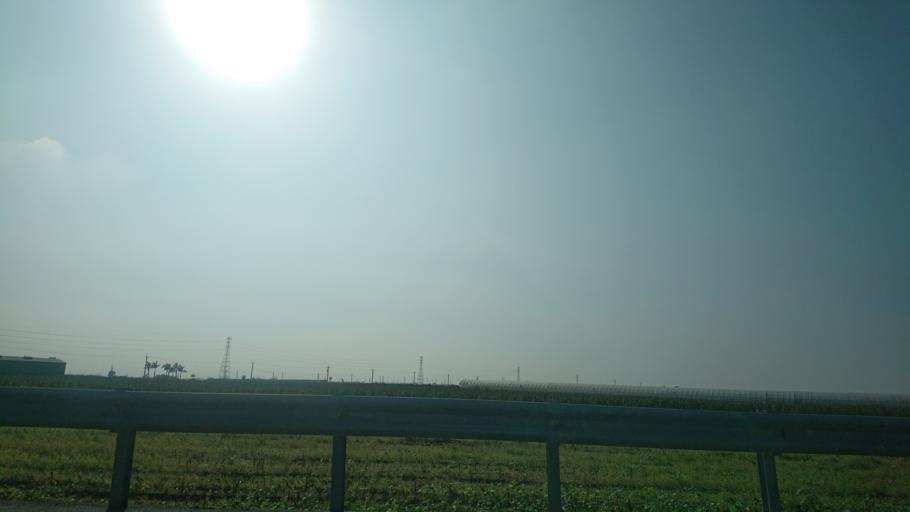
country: TW
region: Taiwan
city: Xinying
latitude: 23.3600
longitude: 120.2521
